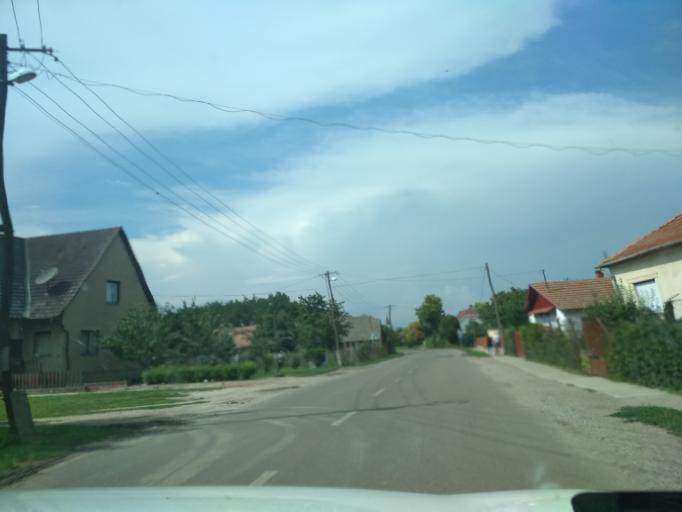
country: HU
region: Jasz-Nagykun-Szolnok
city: Tiszaszolos
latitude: 47.5535
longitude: 20.7199
